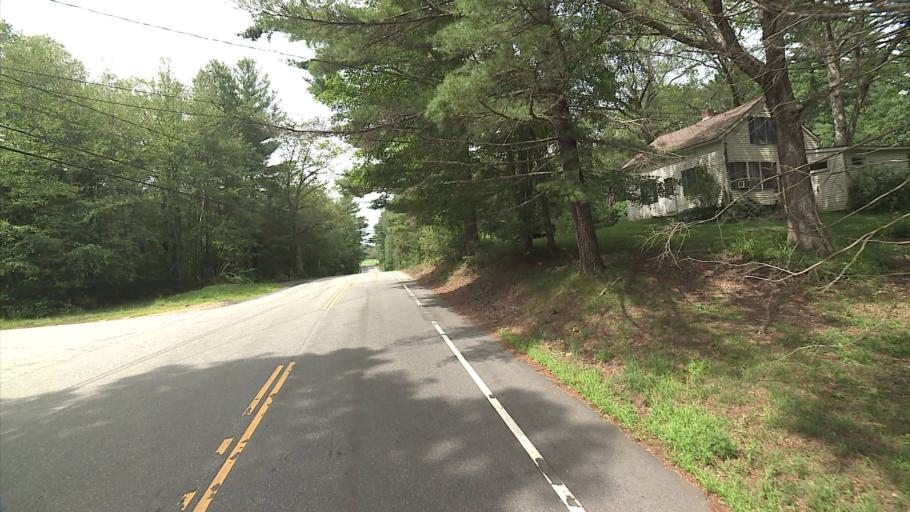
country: US
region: Connecticut
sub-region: Windham County
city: South Woodstock
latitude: 41.9356
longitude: -72.0946
